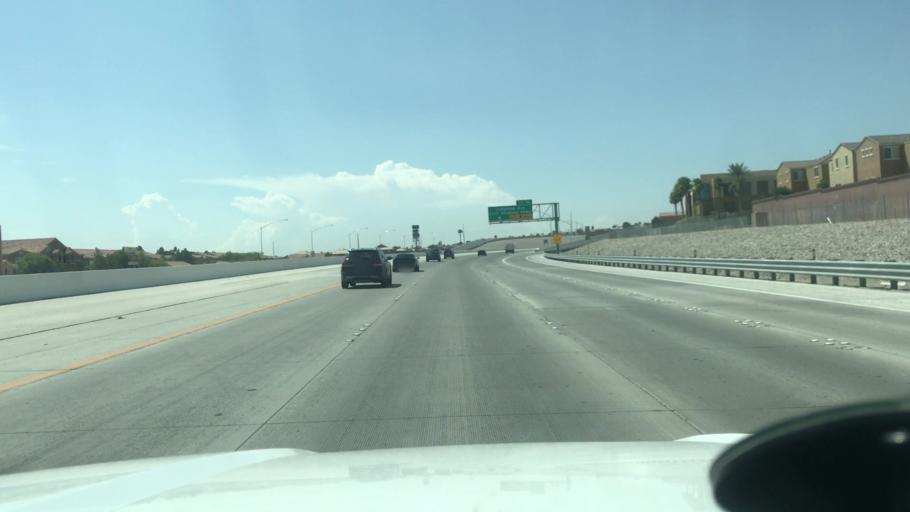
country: US
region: Nevada
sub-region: Clark County
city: Summerlin South
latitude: 36.2264
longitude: -115.3256
